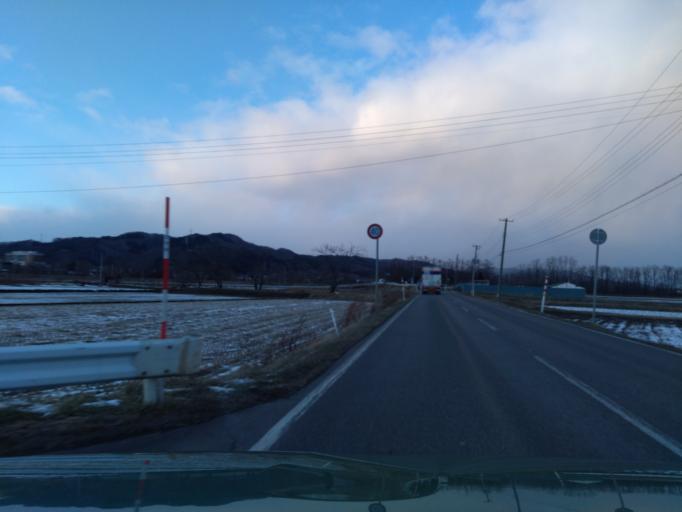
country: JP
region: Iwate
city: Shizukuishi
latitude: 39.6928
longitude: 141.0651
